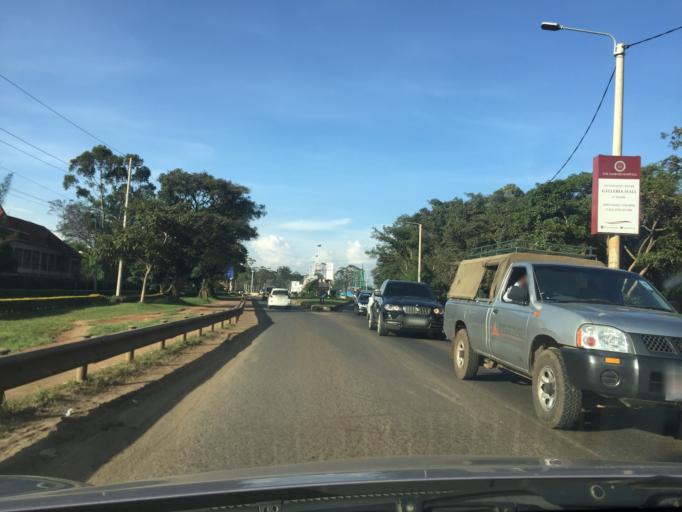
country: KE
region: Nairobi Area
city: Nairobi
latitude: -1.3458
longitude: 36.7657
